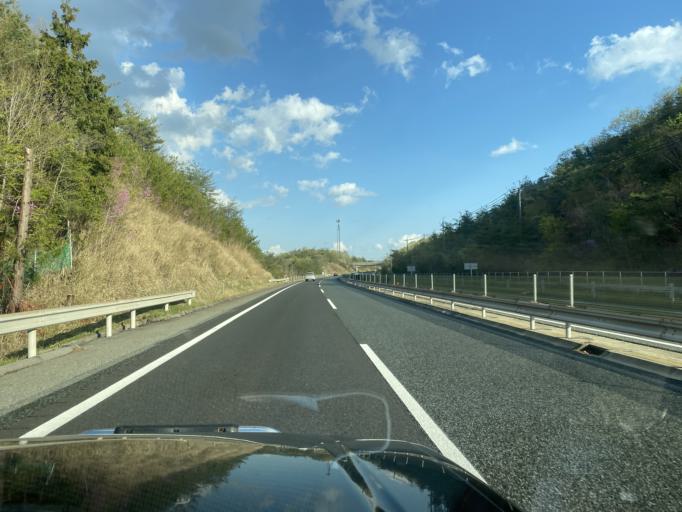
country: JP
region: Hyogo
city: Sandacho
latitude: 34.9556
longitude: 135.1358
